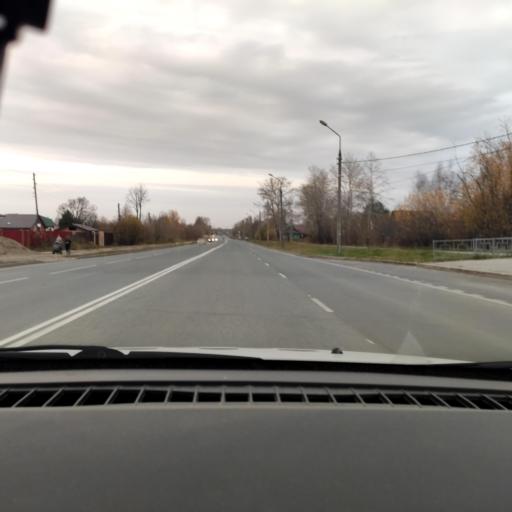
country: RU
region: Perm
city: Polazna
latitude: 58.1175
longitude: 56.4021
